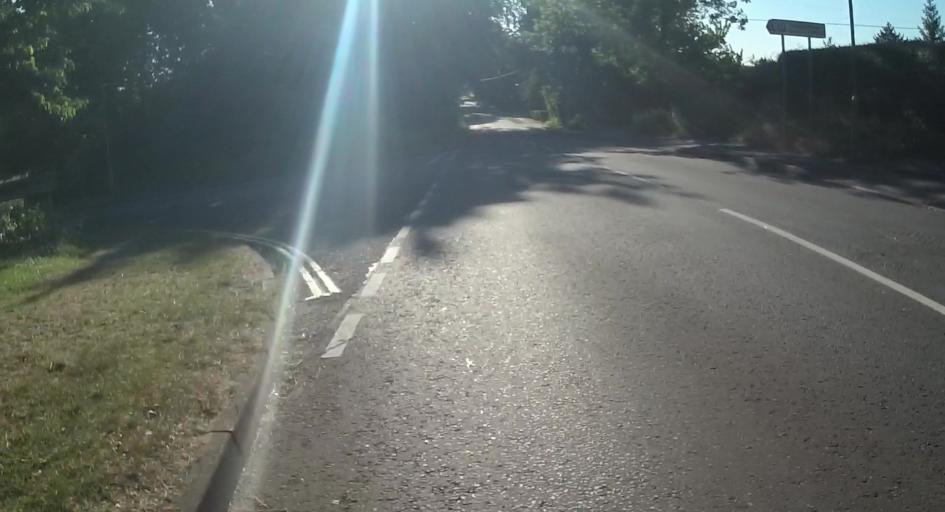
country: GB
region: England
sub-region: Hampshire
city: Basingstoke
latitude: 51.2498
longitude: -1.1263
